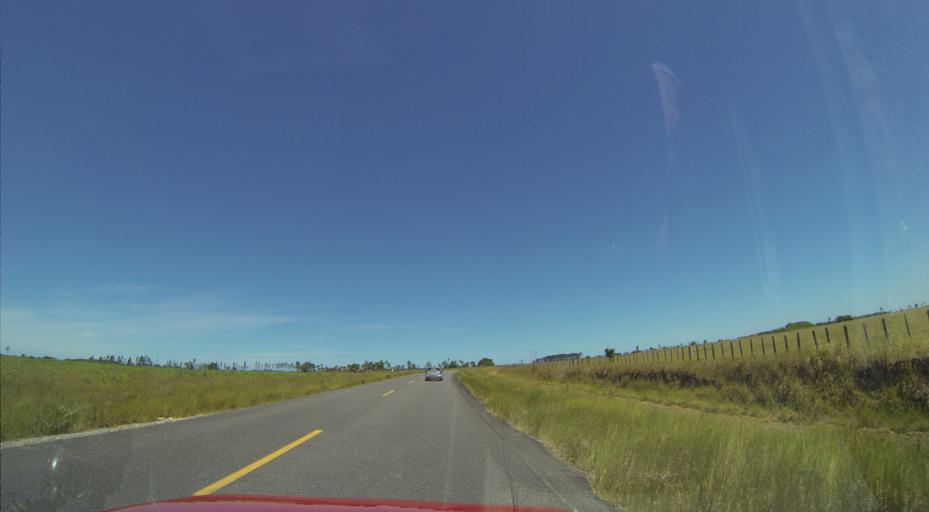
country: BR
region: Bahia
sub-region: Prado
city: Prado
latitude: -17.2246
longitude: -39.3803
